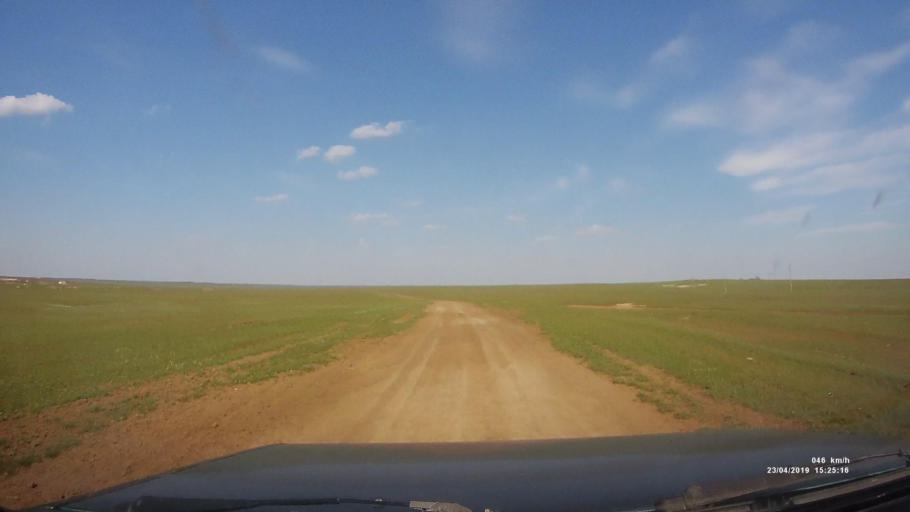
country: RU
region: Rostov
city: Remontnoye
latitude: 46.5411
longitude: 42.9797
